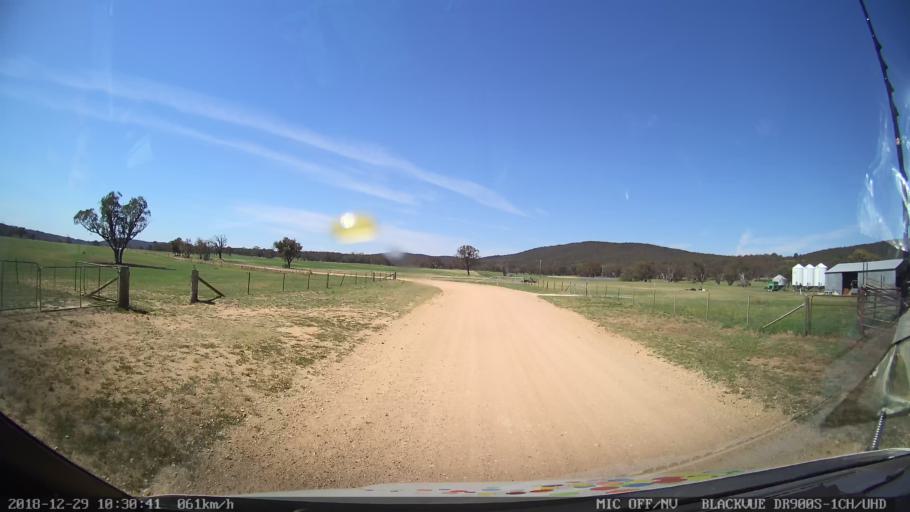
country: AU
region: New South Wales
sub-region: Yass Valley
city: Gundaroo
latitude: -34.9632
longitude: 149.4543
